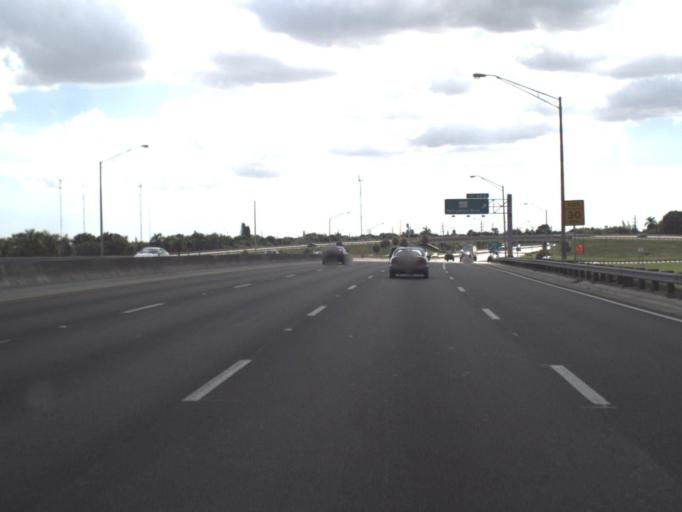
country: US
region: Florida
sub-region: Broward County
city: Pembroke Pines
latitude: 26.0097
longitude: -80.2134
